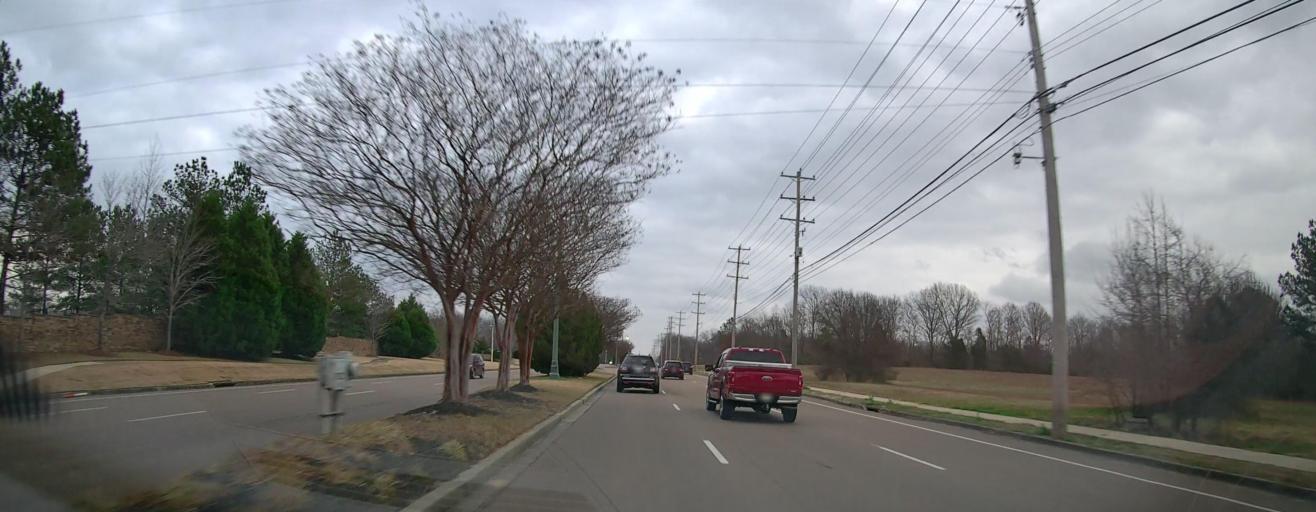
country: US
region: Tennessee
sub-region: Shelby County
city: Germantown
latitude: 35.0475
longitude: -89.7552
